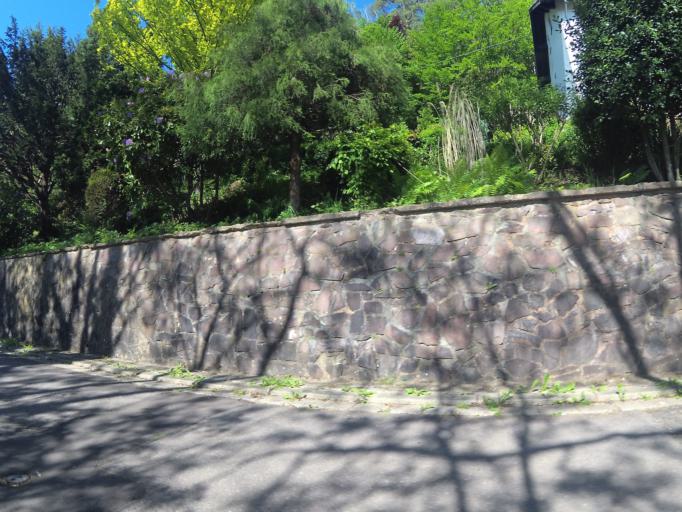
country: DE
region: Saarland
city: Mettlach
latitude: 49.4957
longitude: 6.6043
